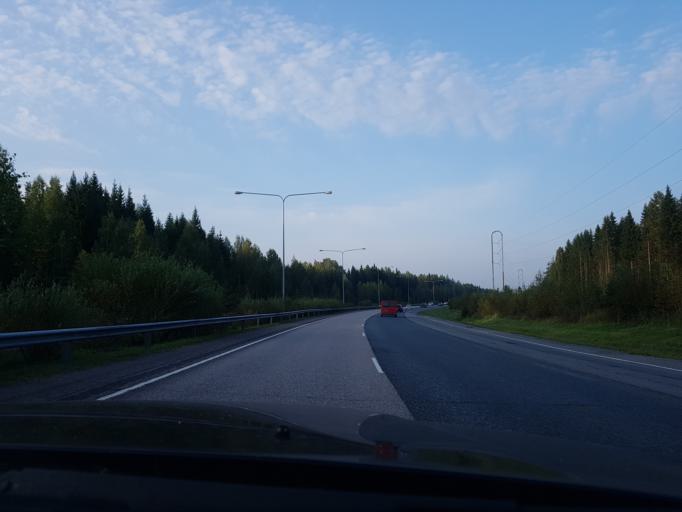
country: FI
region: Uusimaa
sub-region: Helsinki
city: Tuusula
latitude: 60.3599
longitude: 25.0014
